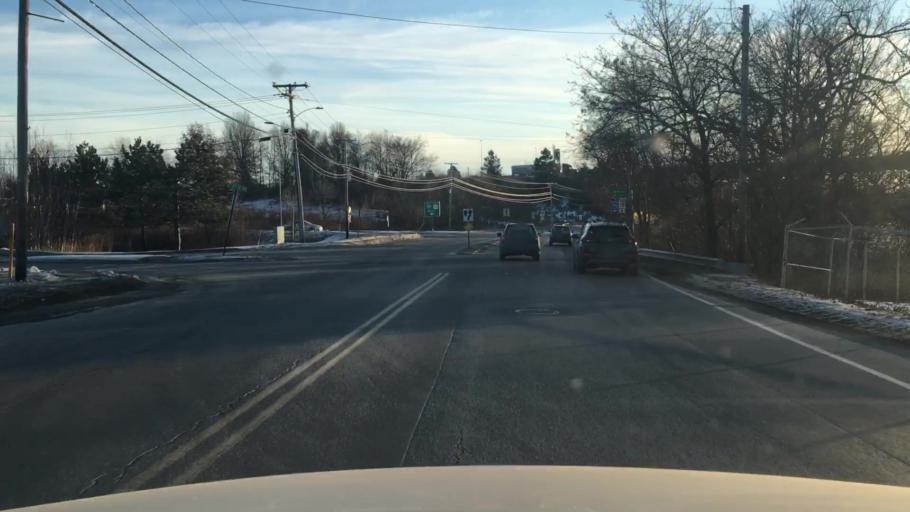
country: US
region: Maine
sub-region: Penobscot County
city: Brewer
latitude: 44.7865
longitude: -68.7709
